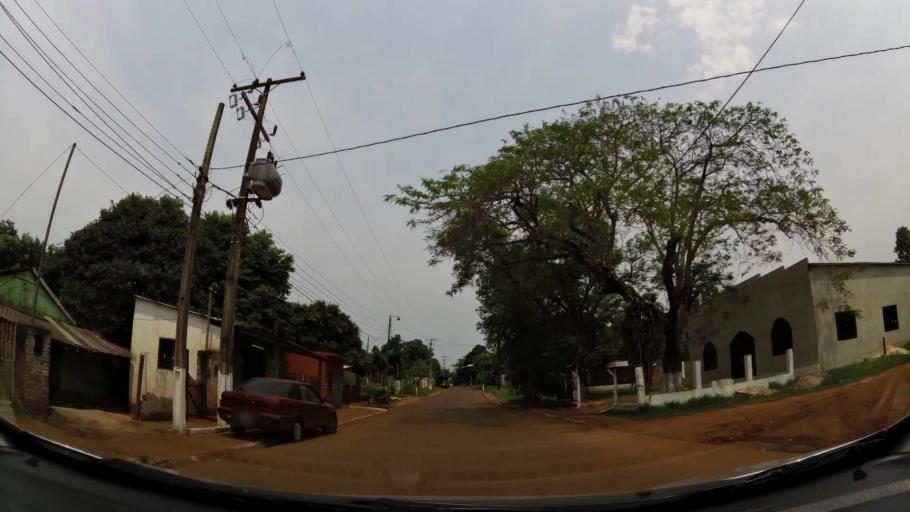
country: BR
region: Parana
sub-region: Foz Do Iguacu
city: Foz do Iguacu
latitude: -25.5709
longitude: -54.6057
